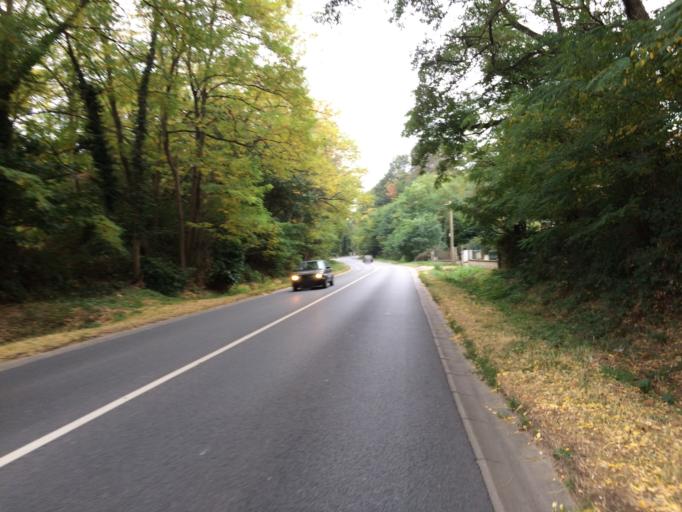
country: FR
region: Ile-de-France
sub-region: Departement de l'Essonne
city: Villebon-sur-Yvette
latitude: 48.6952
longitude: 2.2389
